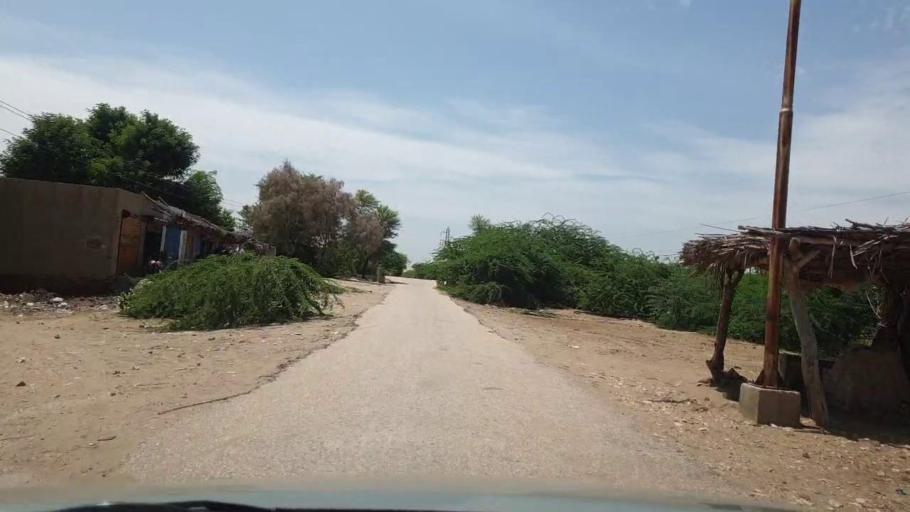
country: PK
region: Sindh
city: Bozdar
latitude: 27.0846
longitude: 68.9663
